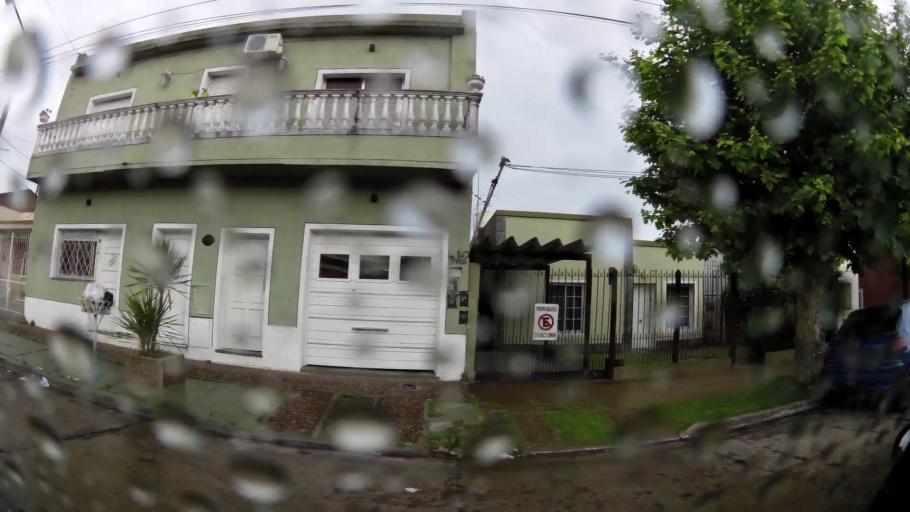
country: AR
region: Buenos Aires
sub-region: Partido de Quilmes
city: Quilmes
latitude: -34.7693
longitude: -58.2215
